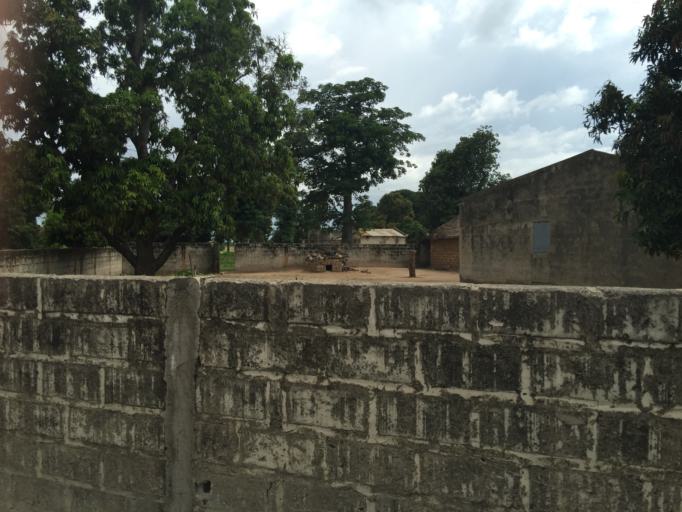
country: SN
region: Fatick
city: Sokone
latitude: 13.7555
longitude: -16.4278
